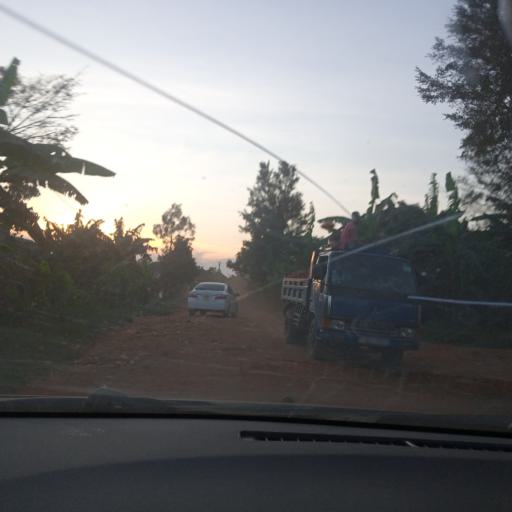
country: UG
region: Central Region
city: Masaka
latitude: -0.3141
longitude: 31.7686
